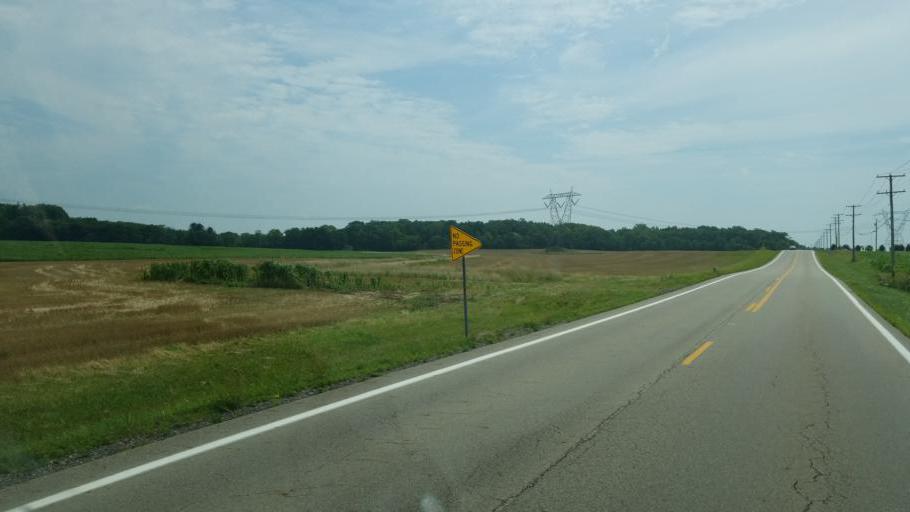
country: US
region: Ohio
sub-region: Madison County
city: Choctaw Lake
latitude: 39.9783
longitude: -83.3887
